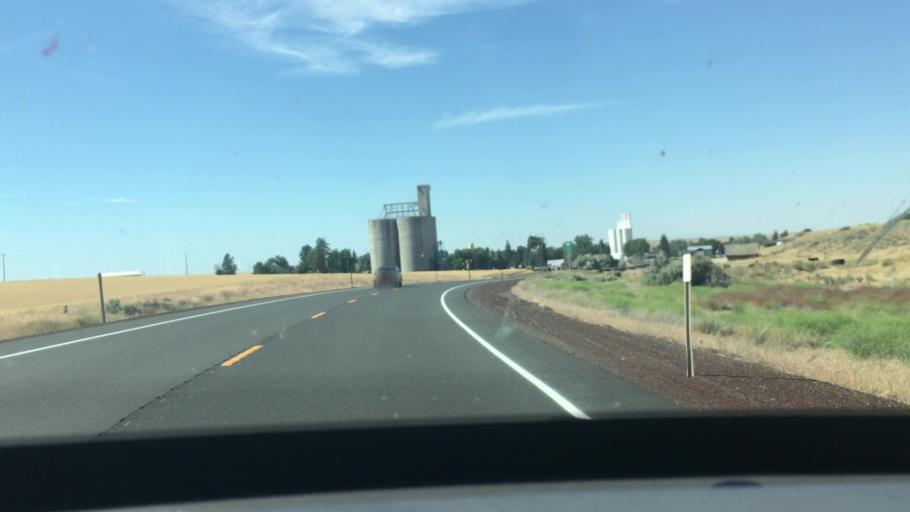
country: US
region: Oregon
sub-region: Sherman County
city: Moro
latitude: 45.3482
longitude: -120.7854
